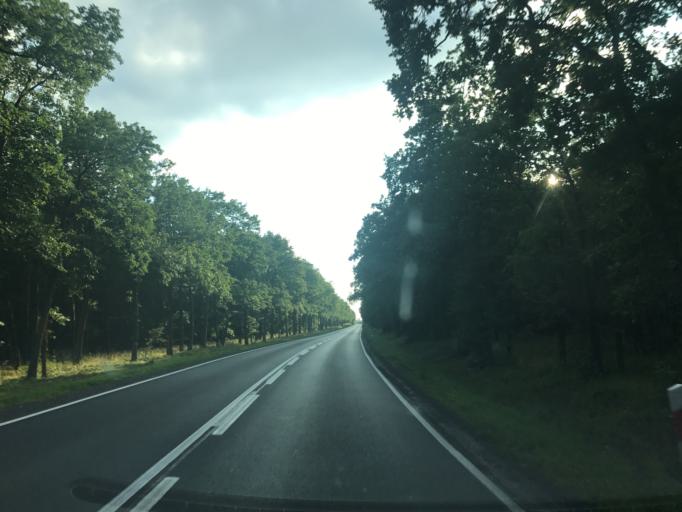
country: PL
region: Greater Poland Voivodeship
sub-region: Powiat jarocinski
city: Jarocin
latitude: 51.9681
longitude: 17.4736
